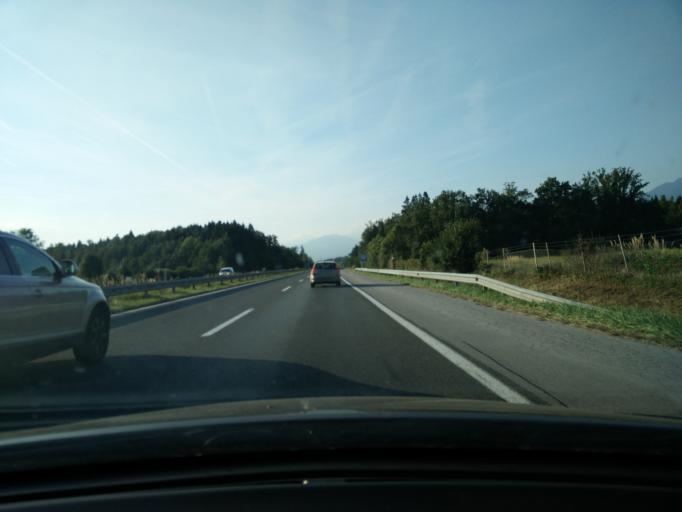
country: SI
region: Kranj
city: Britof
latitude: 46.2422
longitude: 14.3977
